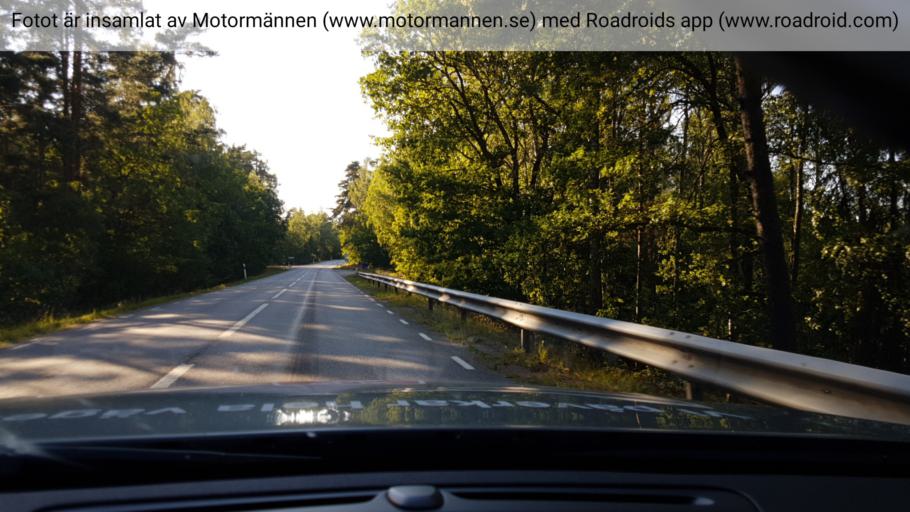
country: SE
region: Vaestmanland
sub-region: Hallstahammars Kommun
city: Hallstahammar
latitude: 59.6552
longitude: 16.1867
